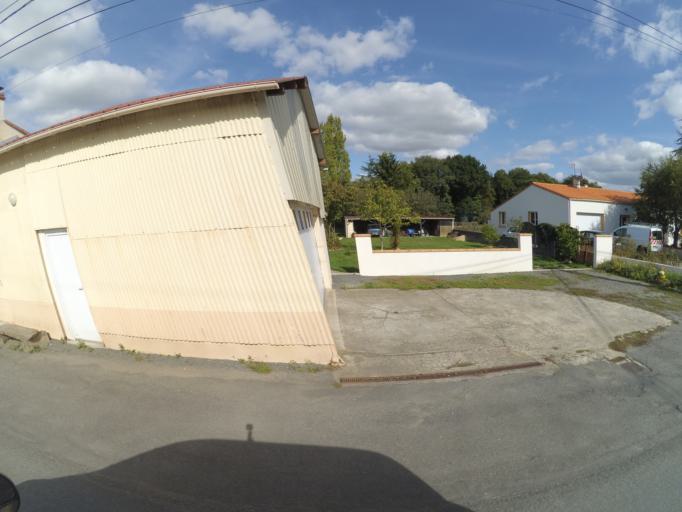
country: FR
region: Pays de la Loire
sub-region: Departement de la Loire-Atlantique
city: Saint-Lumine-de-Clisson
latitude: 47.1079
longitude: -1.3329
